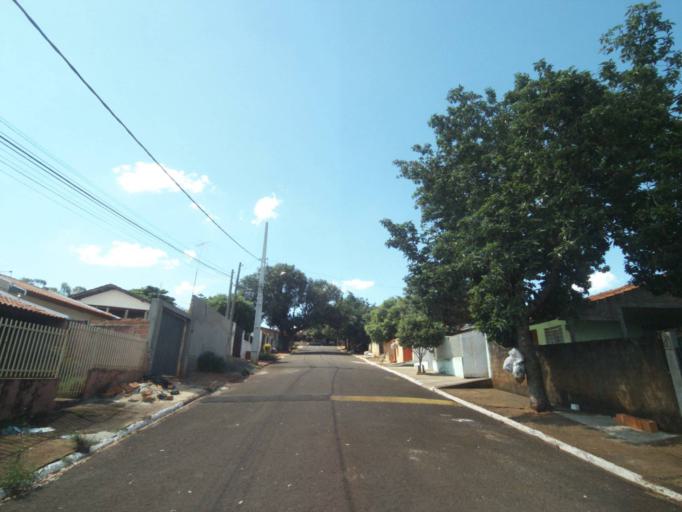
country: BR
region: Parana
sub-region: Sertanopolis
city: Sertanopolis
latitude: -23.0467
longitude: -50.8229
